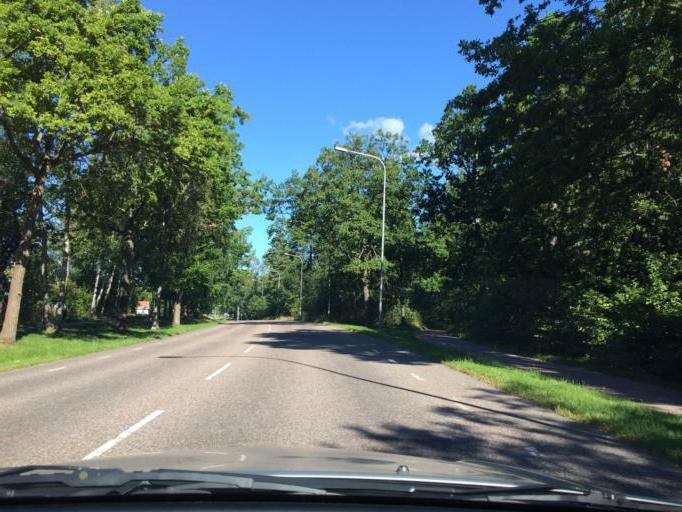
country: SE
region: Vaestmanland
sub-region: Vasteras
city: Vasteras
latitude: 59.5998
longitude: 16.5935
